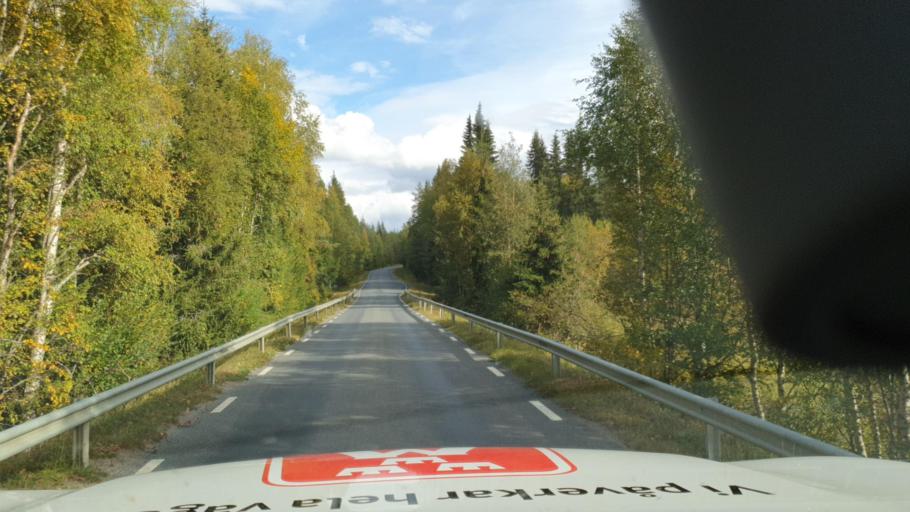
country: SE
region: Dalarna
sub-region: Alvdalens Kommun
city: AElvdalen
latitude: 61.6904
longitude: 13.2625
